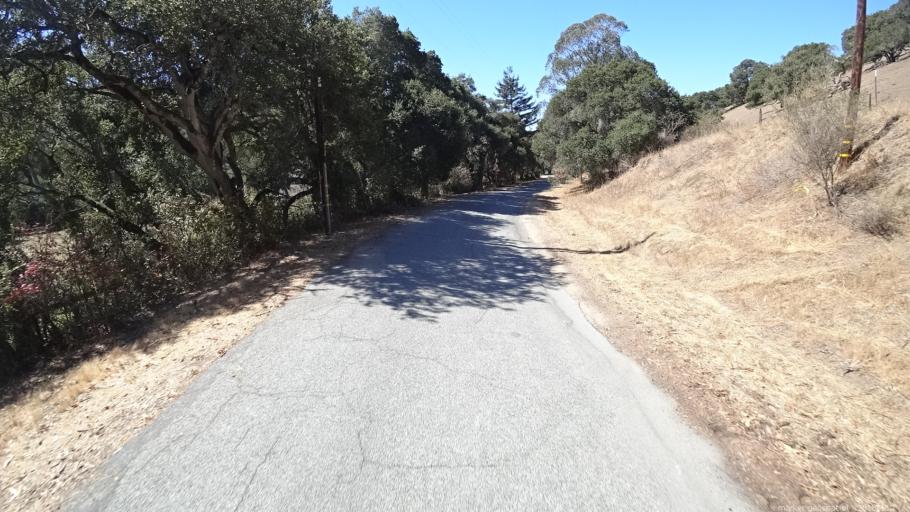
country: US
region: California
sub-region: San Benito County
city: San Juan Bautista
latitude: 36.7982
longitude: -121.5697
